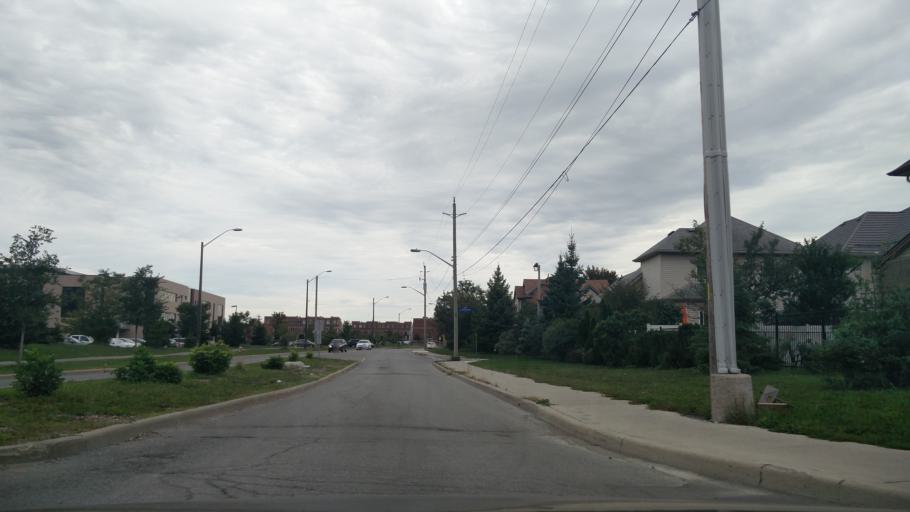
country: CA
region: Ontario
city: Bells Corners
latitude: 45.2806
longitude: -75.7433
